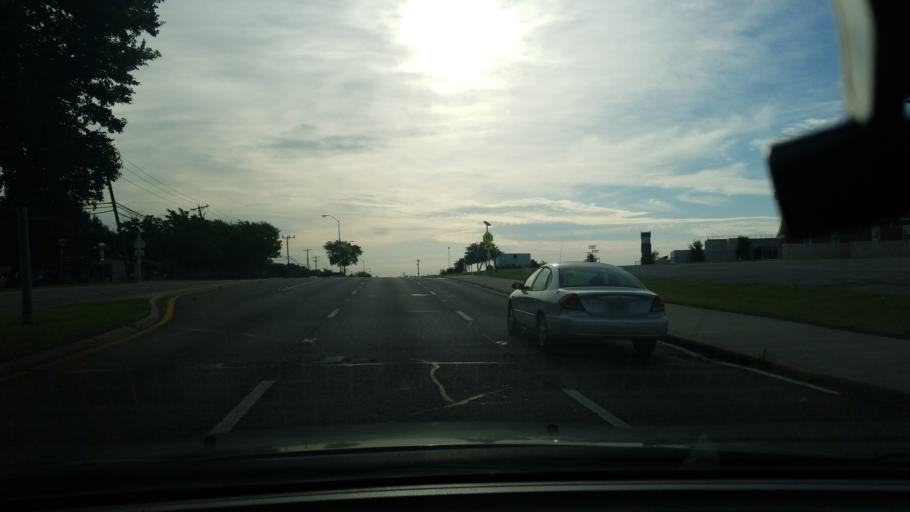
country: US
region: Texas
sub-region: Dallas County
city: Mesquite
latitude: 32.7645
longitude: -96.6369
